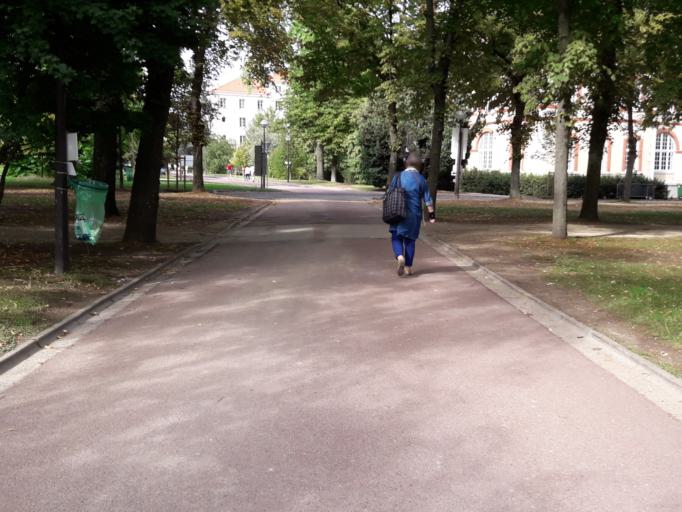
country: FR
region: Ile-de-France
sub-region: Departement du Val-de-Marne
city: Gentilly
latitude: 48.8188
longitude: 2.3363
